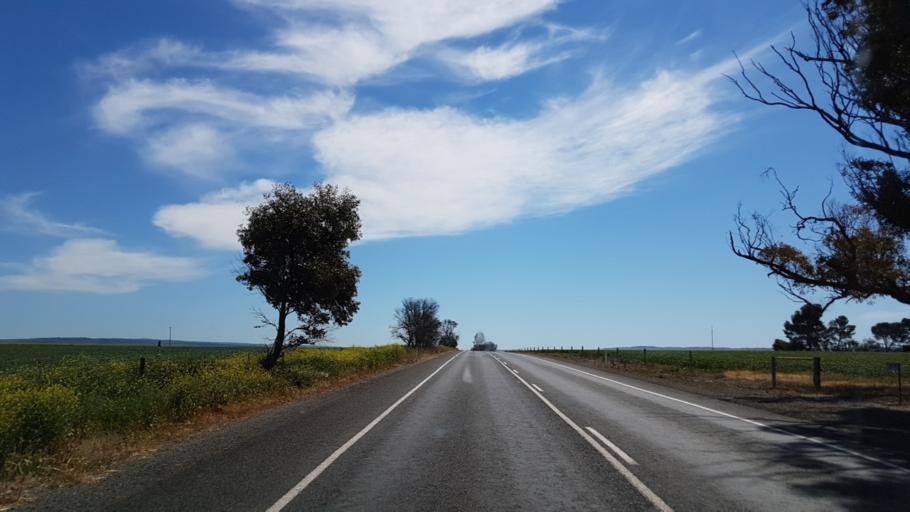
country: AU
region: South Australia
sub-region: Light
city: Freeling
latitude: -34.4087
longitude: 138.7515
